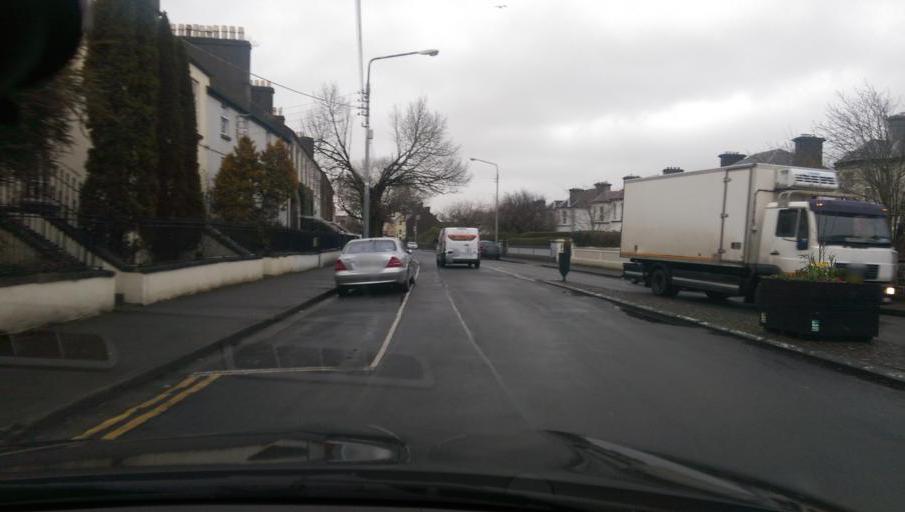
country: IE
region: Connaught
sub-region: County Galway
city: Gaillimh
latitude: 53.2681
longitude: -9.0630
